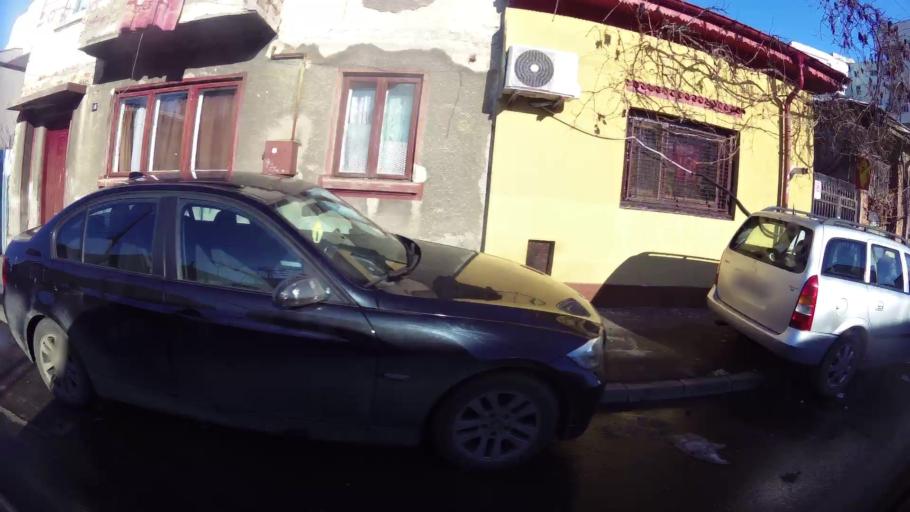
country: RO
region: Bucuresti
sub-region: Municipiul Bucuresti
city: Bucuresti
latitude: 44.4087
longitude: 26.0952
